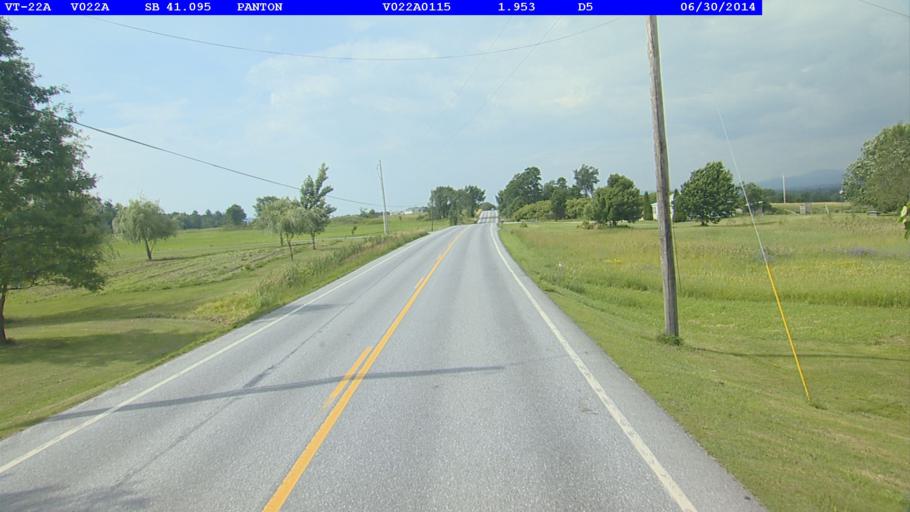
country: US
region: Vermont
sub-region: Addison County
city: Vergennes
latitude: 44.1449
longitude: -73.2766
